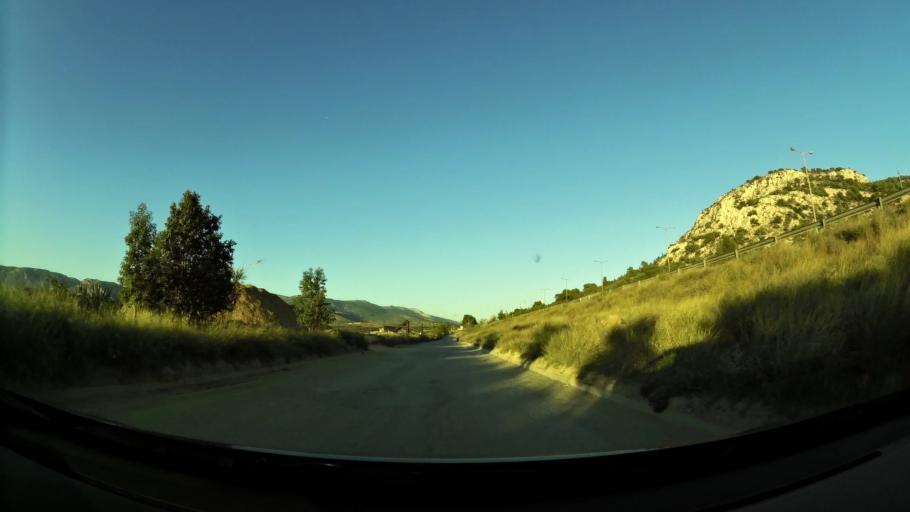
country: GR
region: Attica
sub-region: Nomarchia Athinas
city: Petroupolis
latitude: 38.0476
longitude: 23.6465
